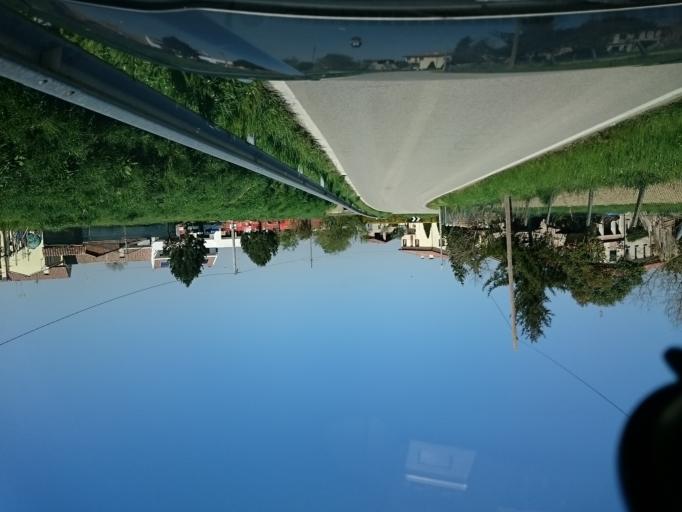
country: IT
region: Veneto
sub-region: Provincia di Padova
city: Albignasego
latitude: 45.3673
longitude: 11.8995
